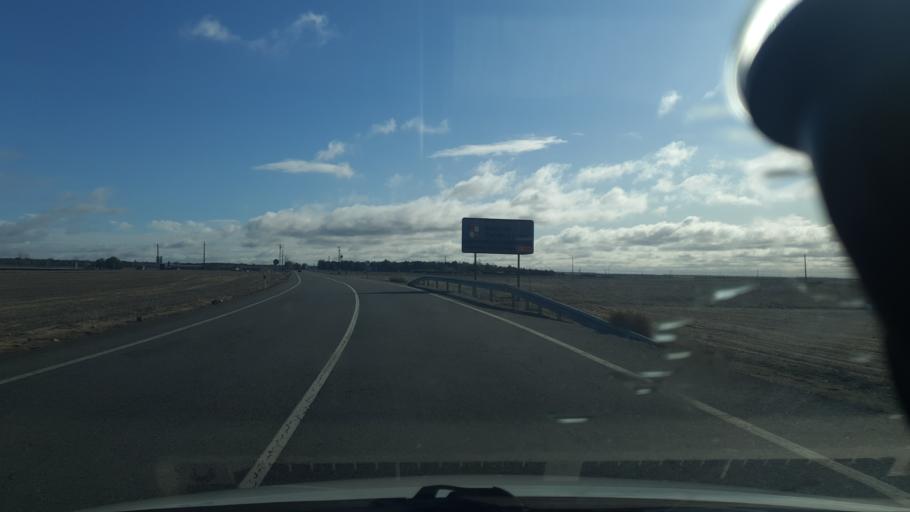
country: ES
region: Castille and Leon
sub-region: Provincia de Segovia
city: Martin Munoz de la Dehesa
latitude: 41.0482
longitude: -4.6936
